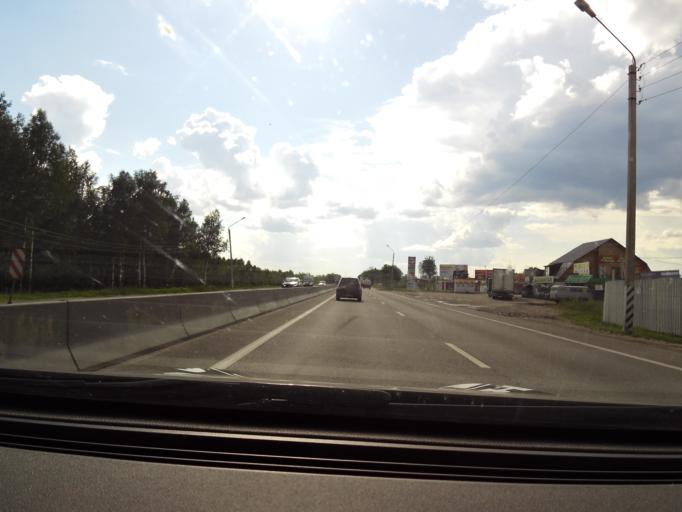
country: RU
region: Nizjnij Novgorod
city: Babino
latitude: 56.3040
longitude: 43.6116
